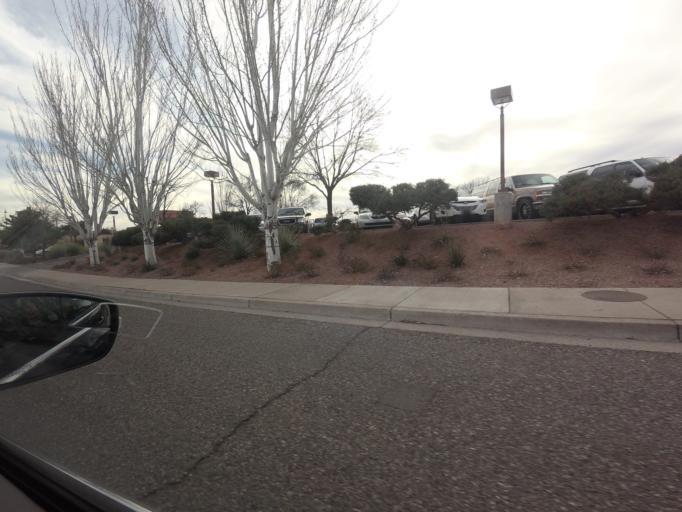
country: US
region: Arizona
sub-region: Yavapai County
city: West Sedona
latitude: 34.8643
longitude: -111.8000
